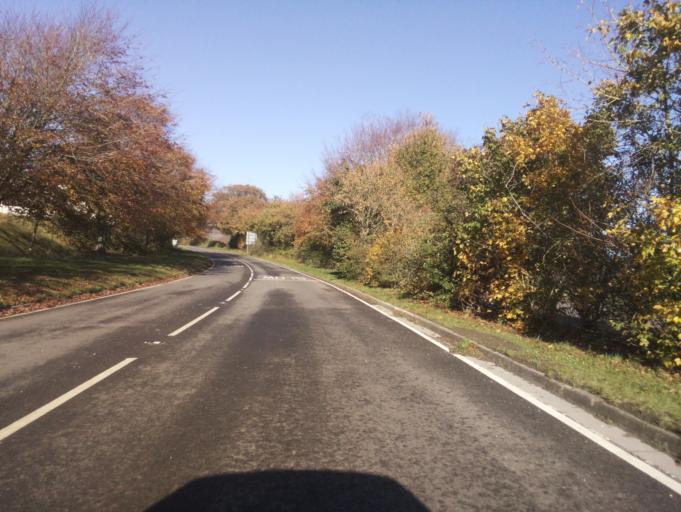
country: GB
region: England
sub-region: Dorset
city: Dorchester
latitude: 50.8131
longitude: -2.4810
